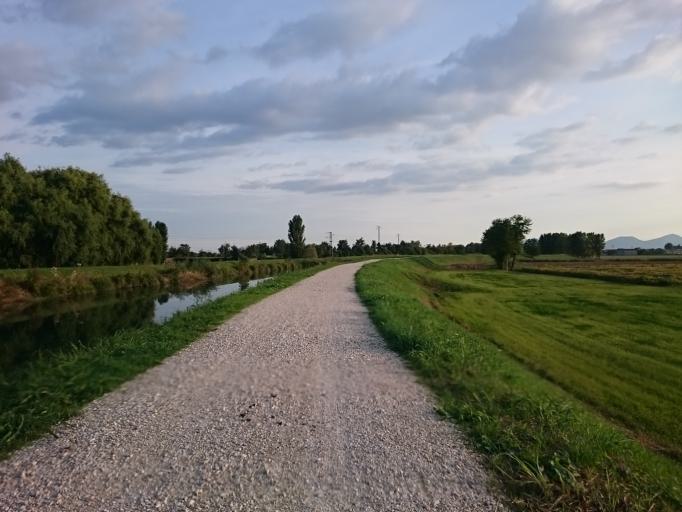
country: IT
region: Veneto
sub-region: Provincia di Padova
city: Campodoro
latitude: 45.4973
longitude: 11.7341
